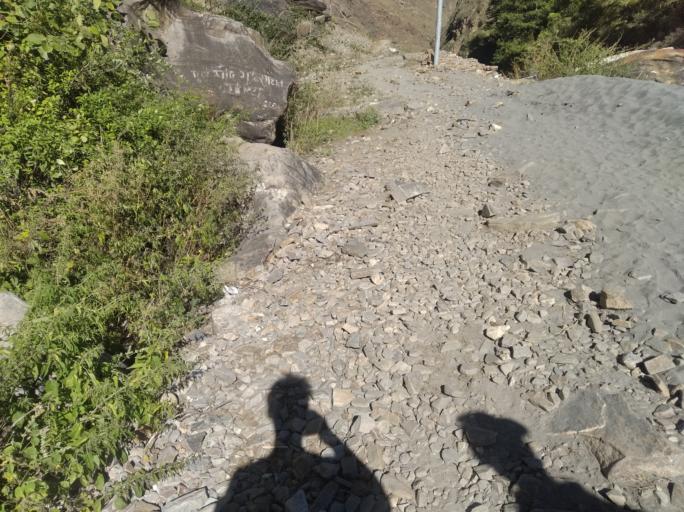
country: NP
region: Western Region
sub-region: Dhawalagiri Zone
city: Jomsom
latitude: 28.9391
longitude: 82.9383
